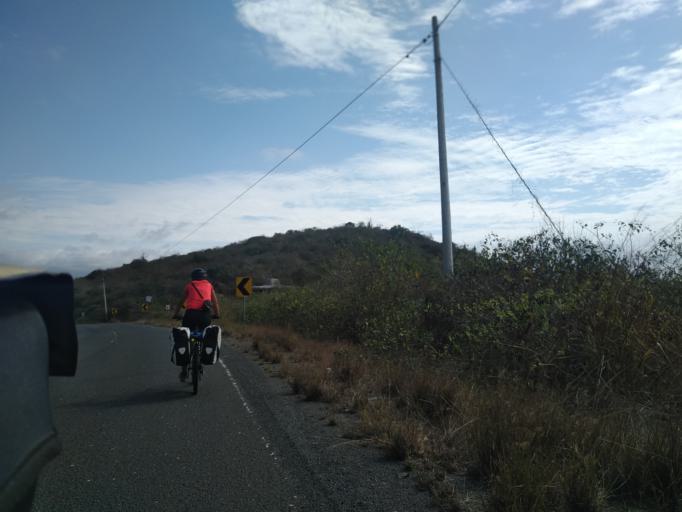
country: EC
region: Manabi
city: Jipijapa
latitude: -1.4473
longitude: -80.7584
